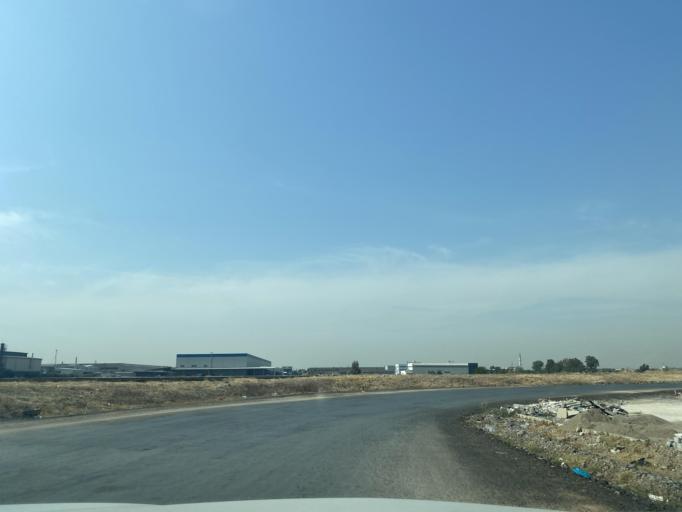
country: TR
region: Izmir
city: Karsiyaka
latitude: 38.4881
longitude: 27.0508
